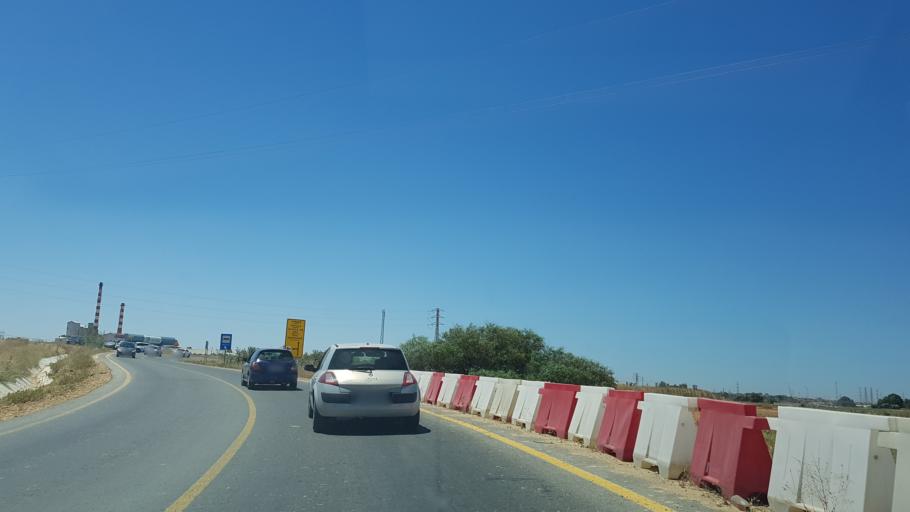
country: ES
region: Andalusia
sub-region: Provincia de Sevilla
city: Dos Hermanas
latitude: 37.3081
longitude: -5.8908
